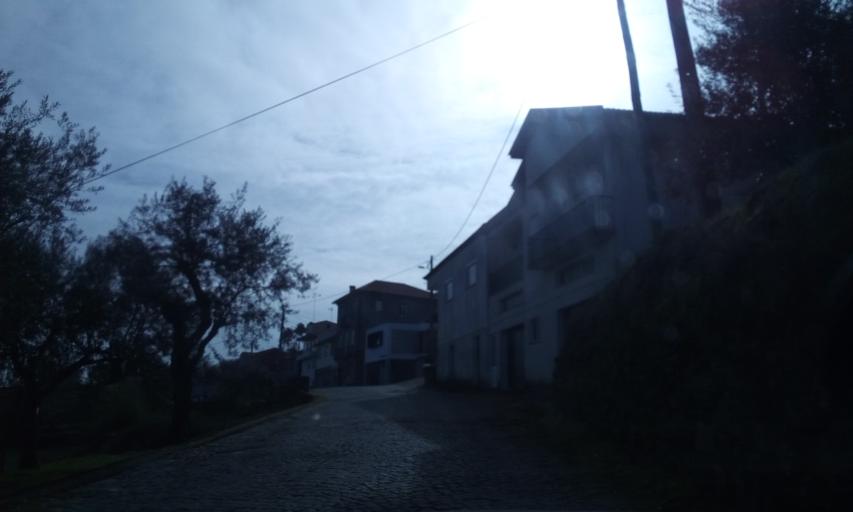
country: PT
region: Guarda
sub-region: Fornos de Algodres
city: Fornos de Algodres
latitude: 40.6873
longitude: -7.5578
